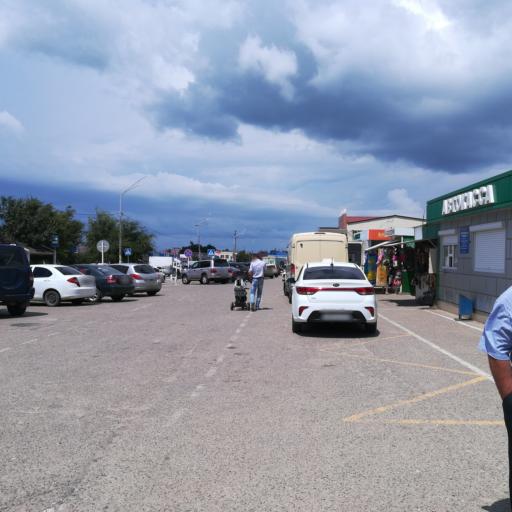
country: RU
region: Krasnodarskiy
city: Taman'
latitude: 45.2142
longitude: 36.7196
